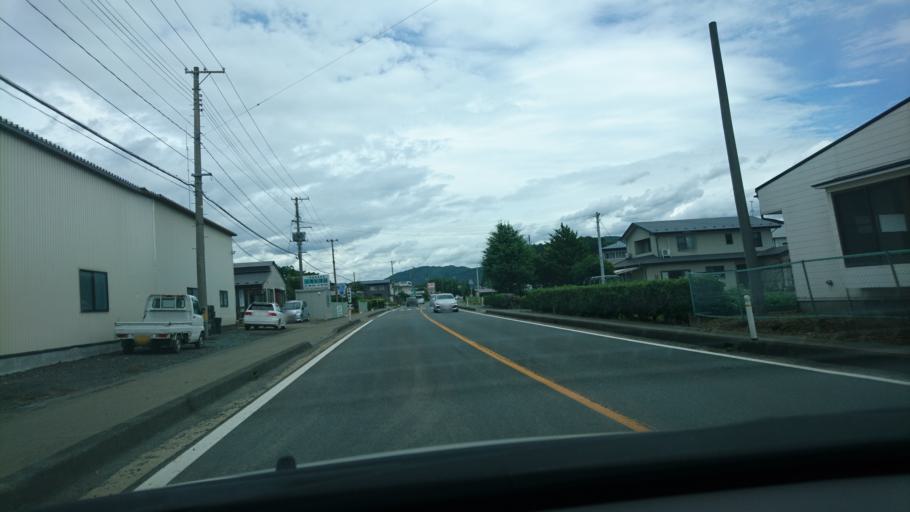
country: JP
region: Iwate
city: Morioka-shi
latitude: 39.6280
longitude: 141.1832
